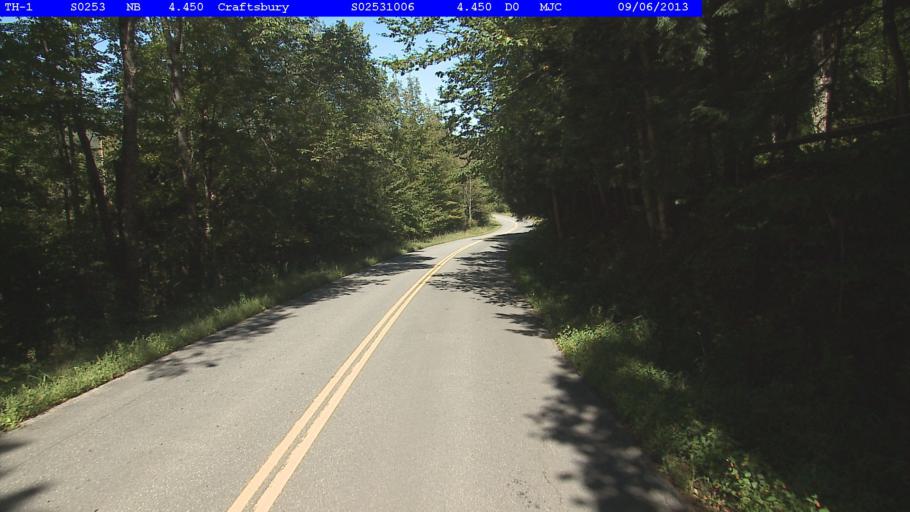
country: US
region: Vermont
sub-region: Caledonia County
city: Hardwick
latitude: 44.6696
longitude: -72.3907
